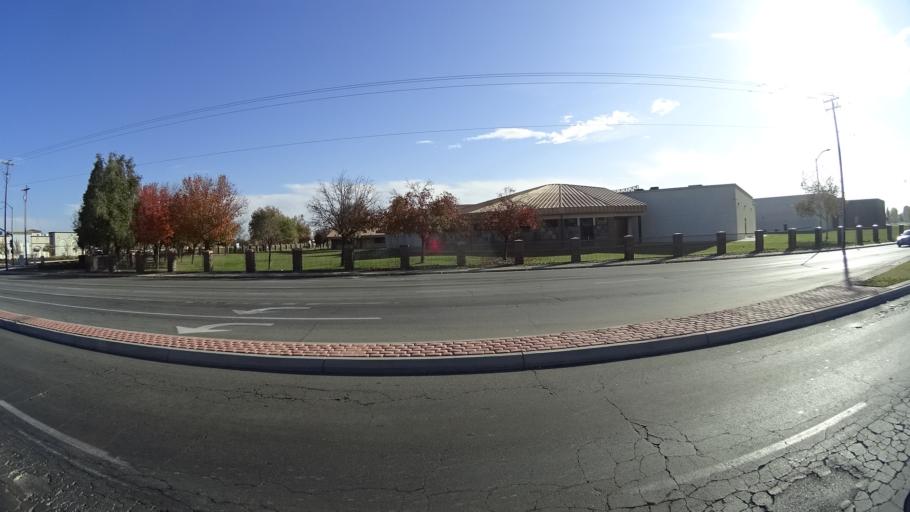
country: US
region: California
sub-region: Kern County
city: Rosedale
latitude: 35.3537
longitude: -119.1457
